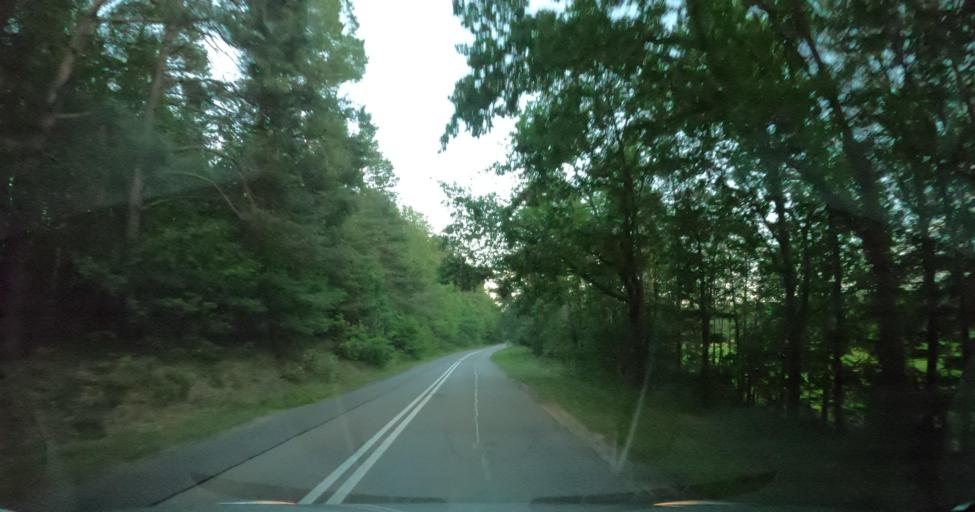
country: PL
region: Pomeranian Voivodeship
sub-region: Powiat wejherowski
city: Linia
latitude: 54.4598
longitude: 18.0013
